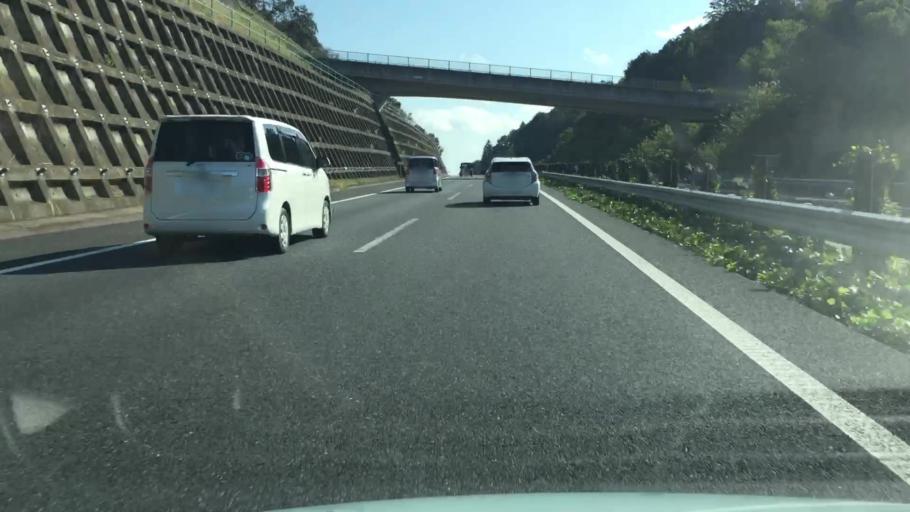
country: JP
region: Ibaraki
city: Kasama
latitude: 36.3425
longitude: 140.1934
